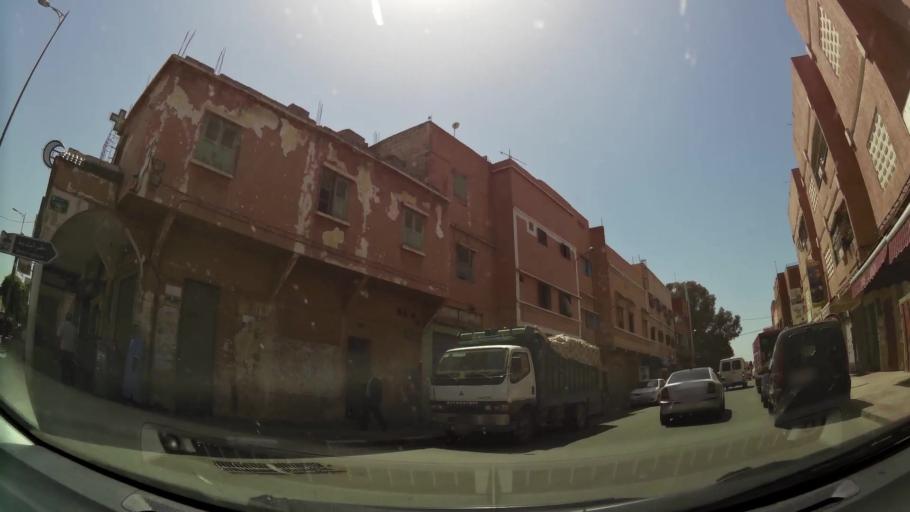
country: MA
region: Souss-Massa-Draa
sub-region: Inezgane-Ait Mellou
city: Inezgane
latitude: 30.3459
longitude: -9.5030
